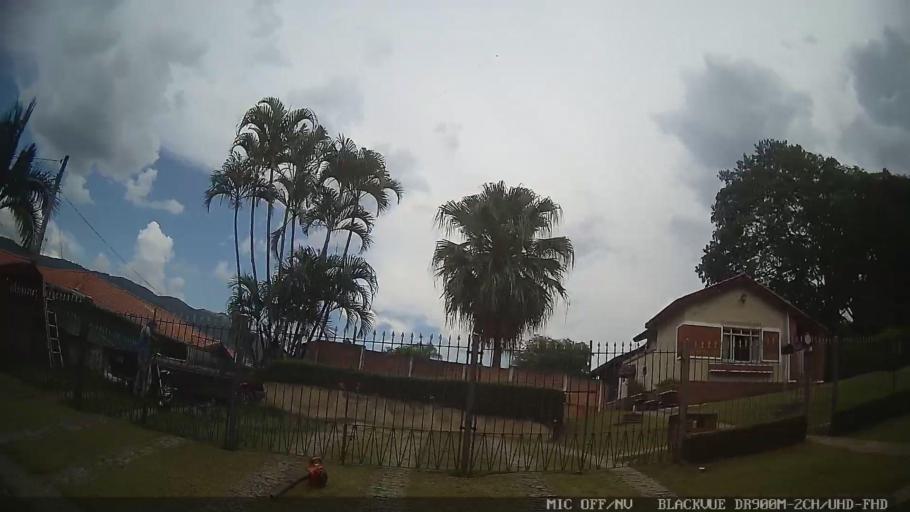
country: BR
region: Sao Paulo
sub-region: Atibaia
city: Atibaia
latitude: -23.1401
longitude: -46.5593
